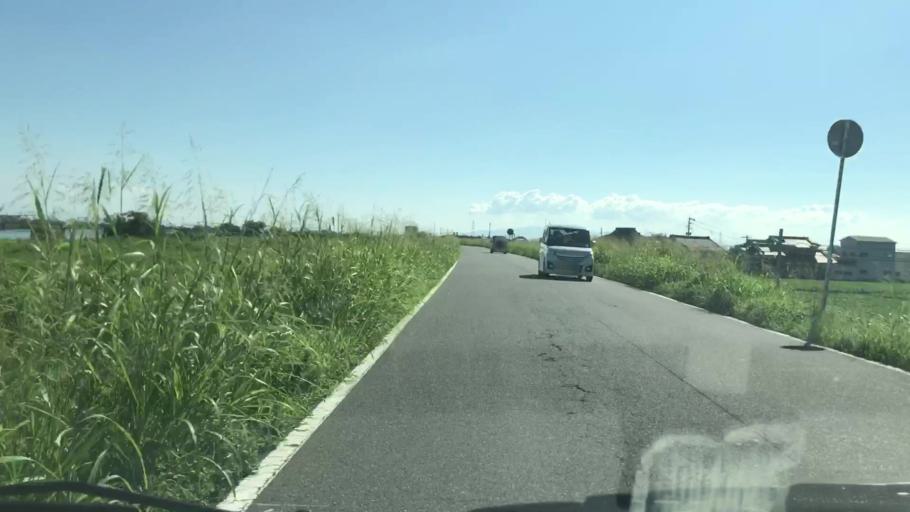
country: JP
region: Saga Prefecture
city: Kanzakimachi-kanzaki
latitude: 33.2681
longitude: 130.4220
